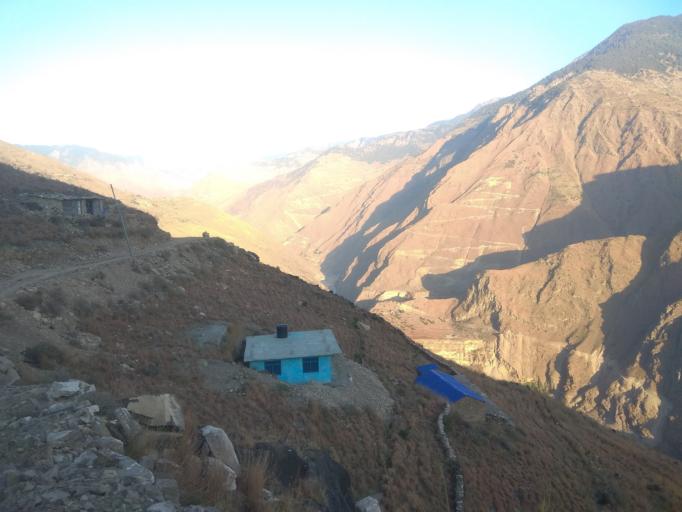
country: NP
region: Mid Western
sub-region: Bheri Zone
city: Dailekh
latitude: 29.2629
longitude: 81.6874
